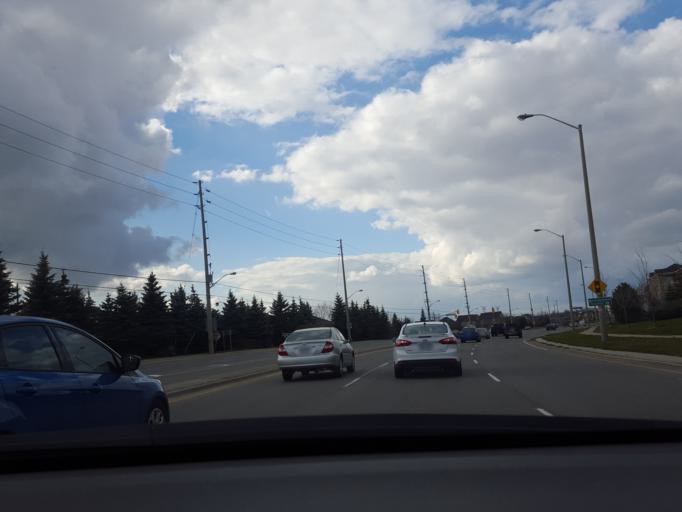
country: CA
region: Ontario
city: Brampton
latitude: 43.6328
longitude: -79.7241
